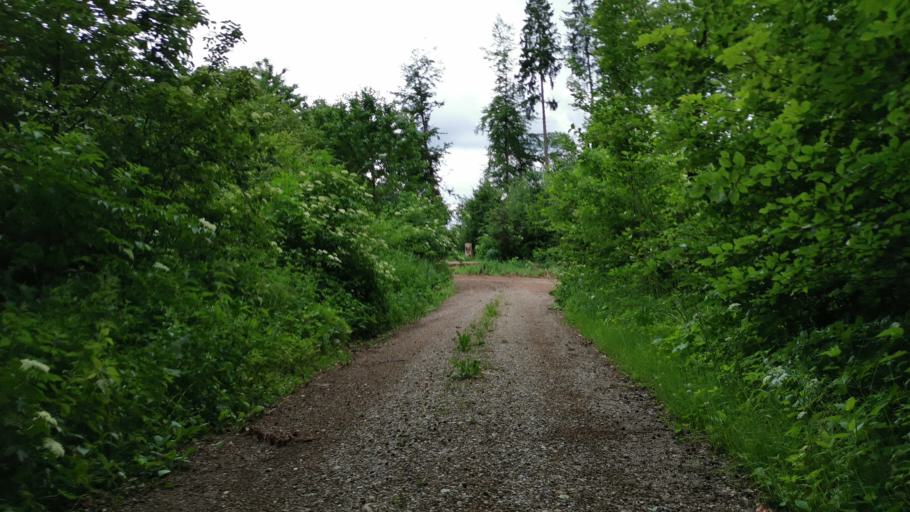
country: DE
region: Bavaria
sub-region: Upper Bavaria
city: Schaftlarn
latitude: 47.9996
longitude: 11.4405
